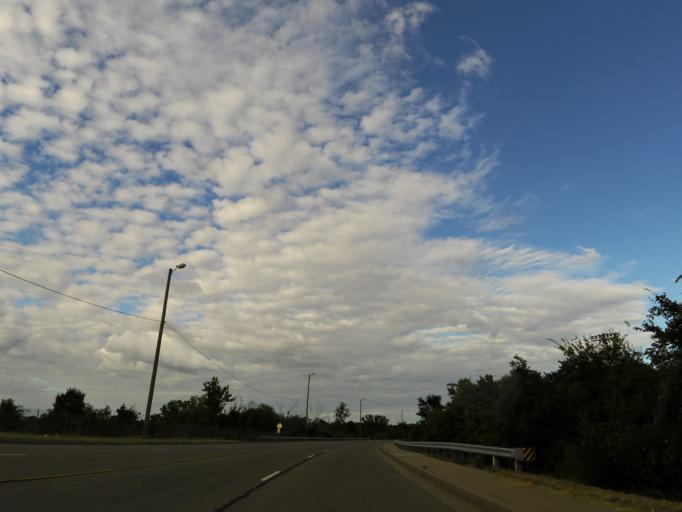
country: US
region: Tennessee
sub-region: Davidson County
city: Nashville
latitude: 36.1714
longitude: -86.8310
